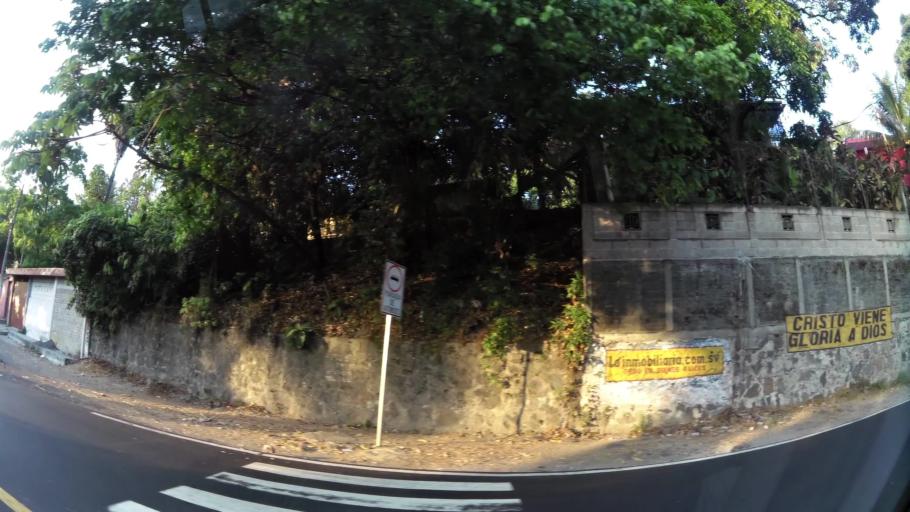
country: SV
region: San Salvador
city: San Salvador
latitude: 13.6863
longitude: -89.2100
